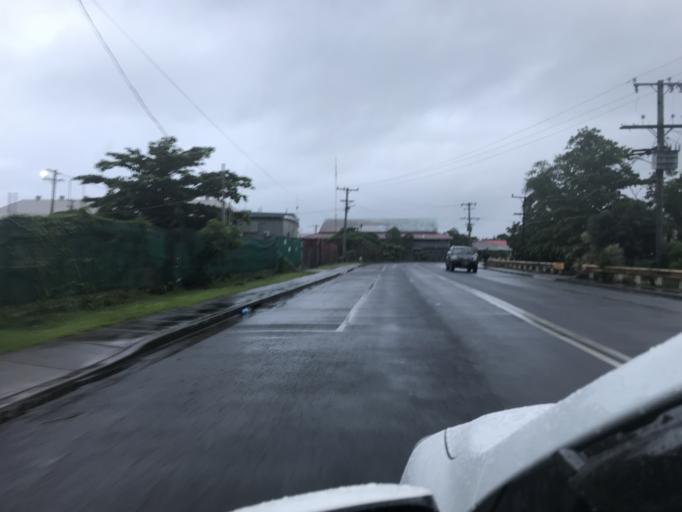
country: WS
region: Tuamasaga
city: Apia
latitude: -13.8336
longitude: -171.7650
